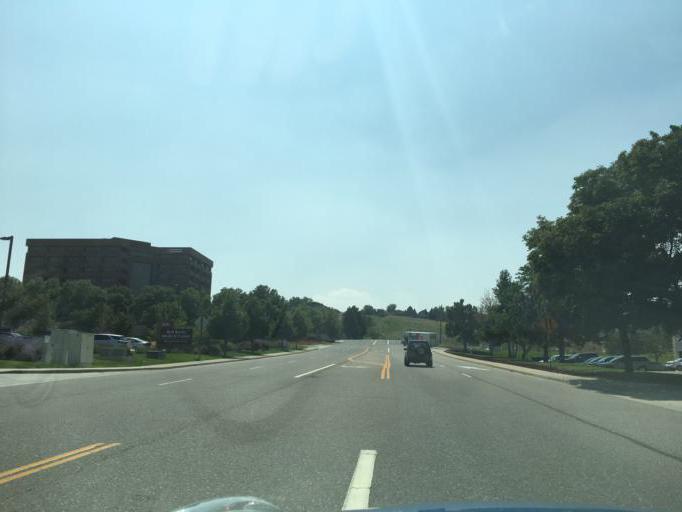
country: US
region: Colorado
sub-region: Jefferson County
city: West Pleasant View
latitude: 39.7231
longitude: -105.1655
